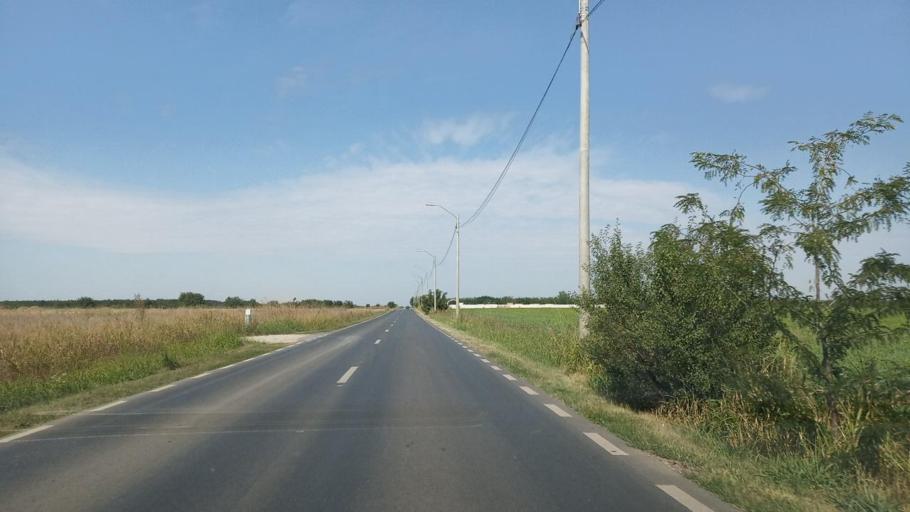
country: RO
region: Ilfov
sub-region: Comuna Tunari
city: Tunari
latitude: 44.5626
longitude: 26.1420
